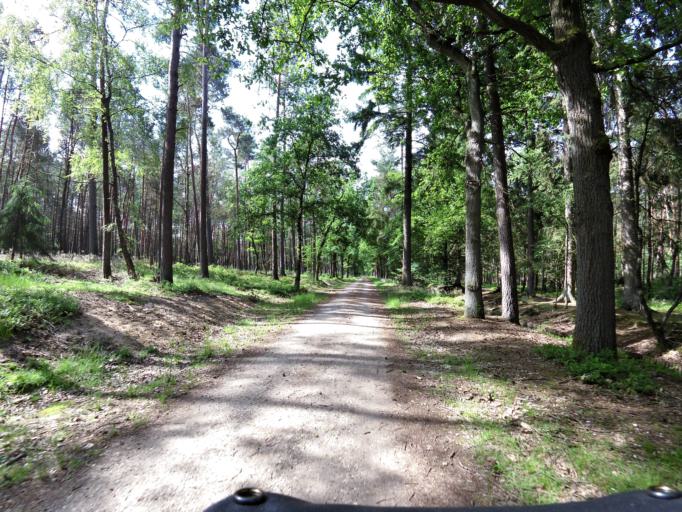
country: NL
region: Gelderland
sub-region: Gemeente Apeldoorn
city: Loenen
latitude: 52.1220
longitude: 5.9975
